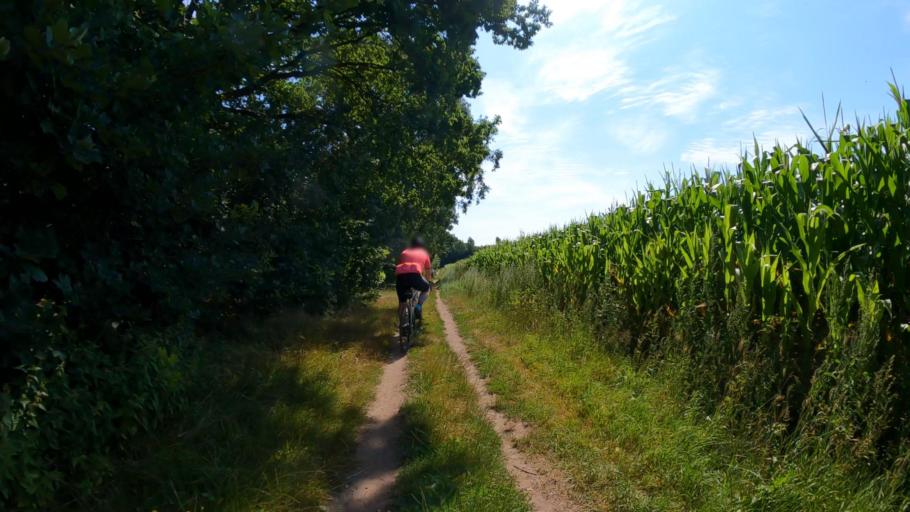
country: DE
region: Schleswig-Holstein
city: Boostedt
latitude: 54.0482
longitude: 10.0340
